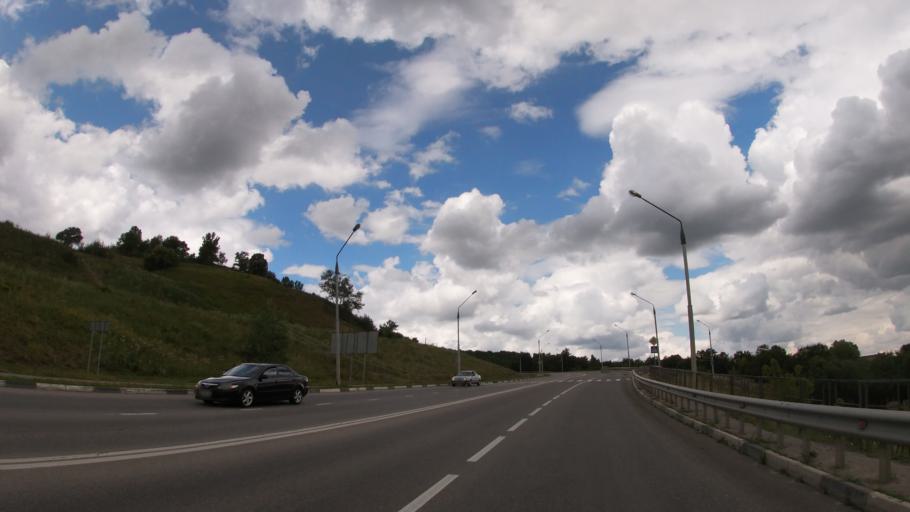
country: RU
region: Belgorod
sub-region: Belgorodskiy Rayon
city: Belgorod
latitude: 50.6185
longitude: 36.6163
